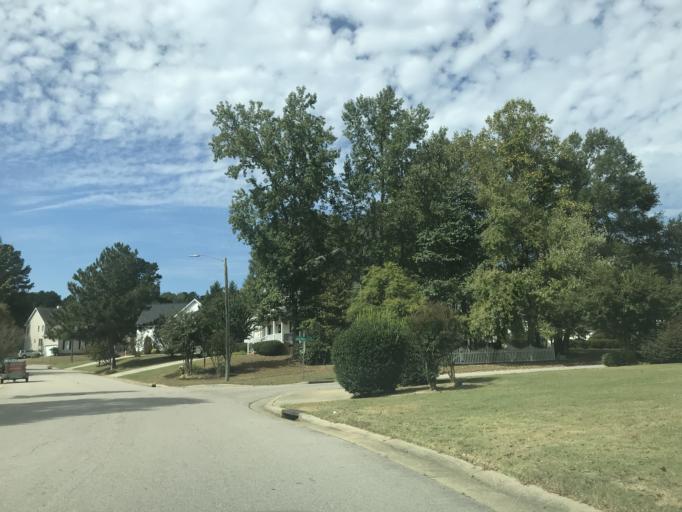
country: US
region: North Carolina
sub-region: Wake County
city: Rolesville
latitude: 35.8718
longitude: -78.5414
